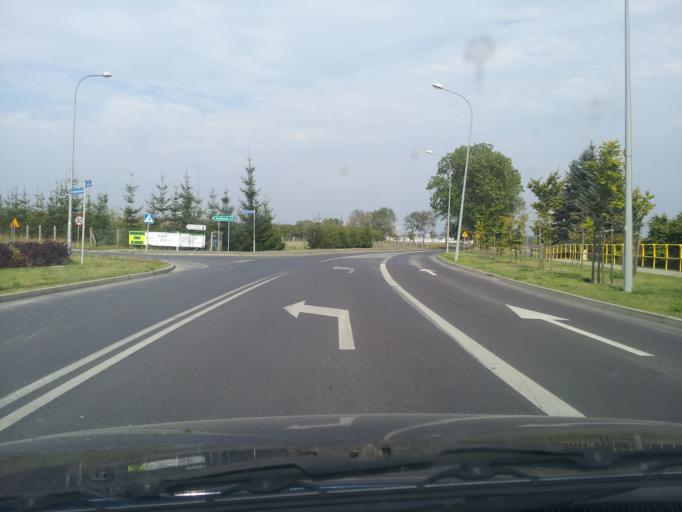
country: PL
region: Warmian-Masurian Voivodeship
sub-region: Powiat ilawski
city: Ilawa
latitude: 53.6106
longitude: 19.5704
